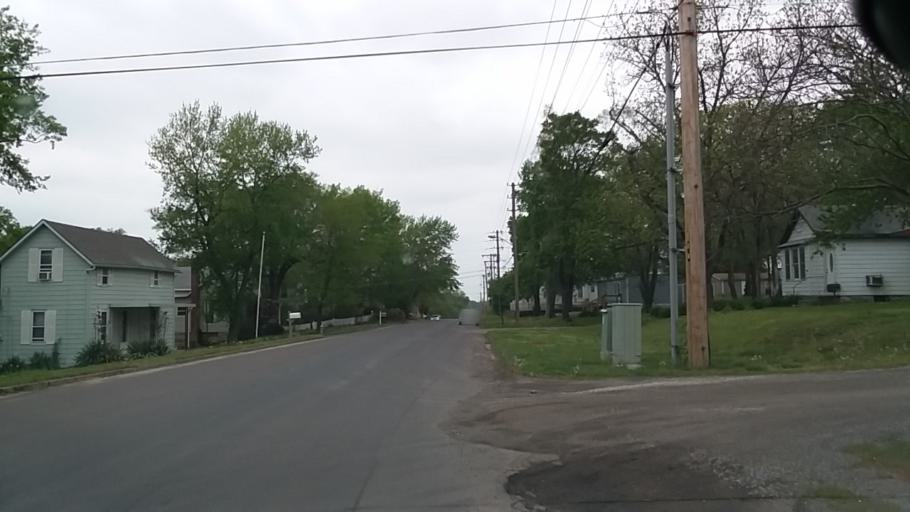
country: US
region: Kansas
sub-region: Douglas County
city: Eudora
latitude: 38.9467
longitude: -95.0963
